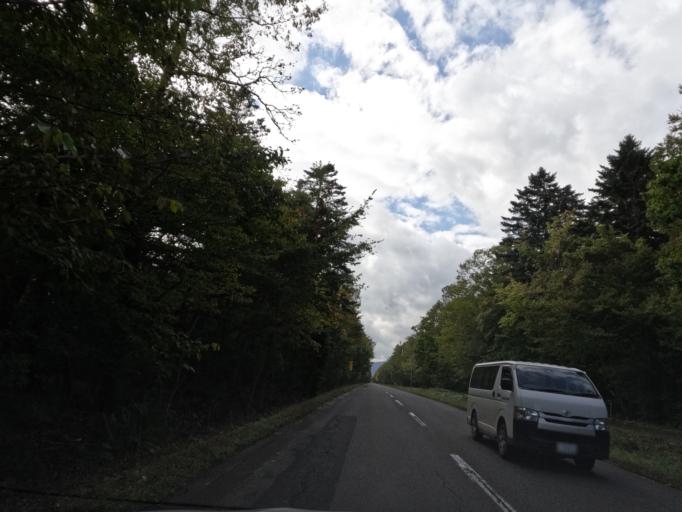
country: JP
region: Hokkaido
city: Chitose
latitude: 42.7918
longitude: 141.5429
